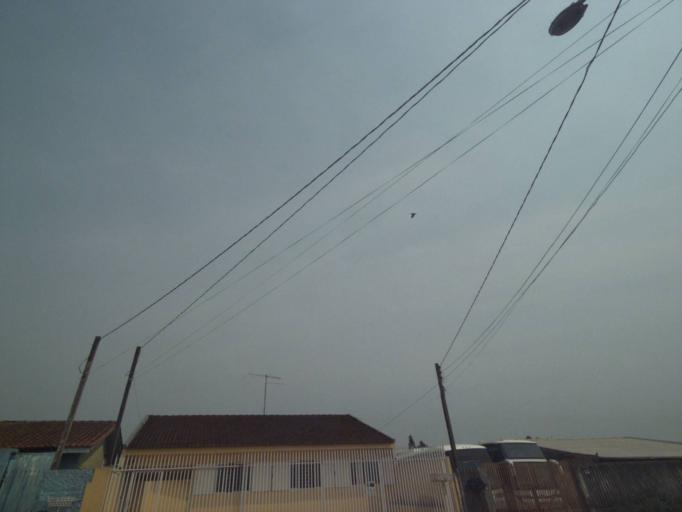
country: BR
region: Parana
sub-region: Sao Jose Dos Pinhais
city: Sao Jose dos Pinhais
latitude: -25.5208
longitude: -49.2875
